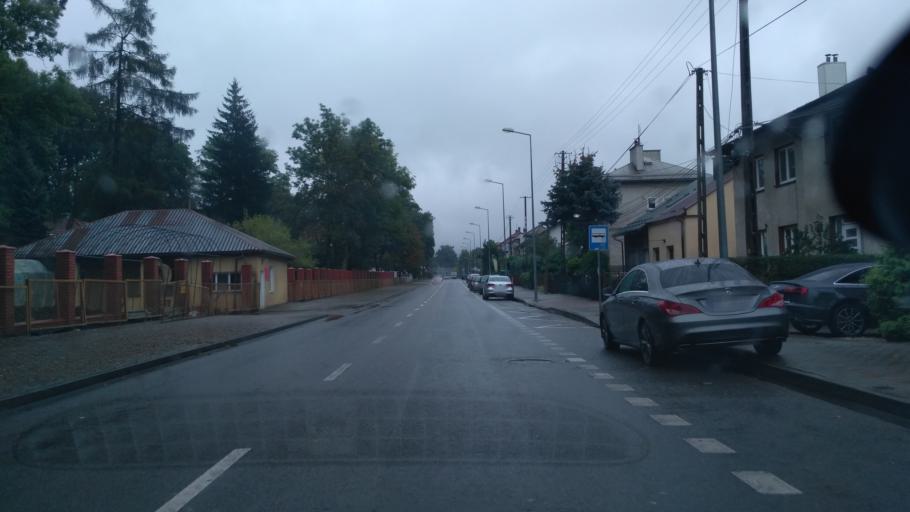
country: PL
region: Subcarpathian Voivodeship
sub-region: Powiat debicki
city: Debica
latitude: 50.0604
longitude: 21.4066
